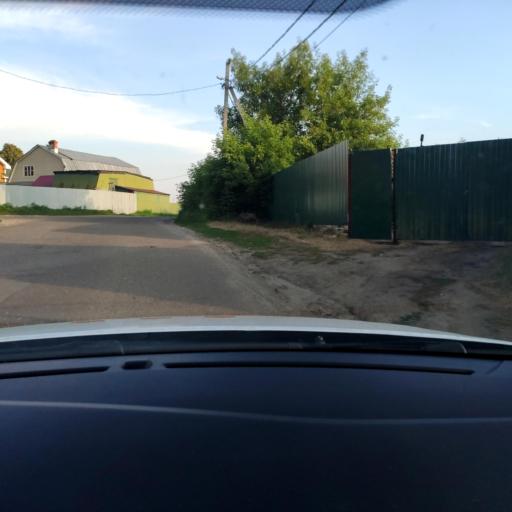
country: RU
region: Tatarstan
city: Vysokaya Gora
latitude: 55.9760
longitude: 49.3061
